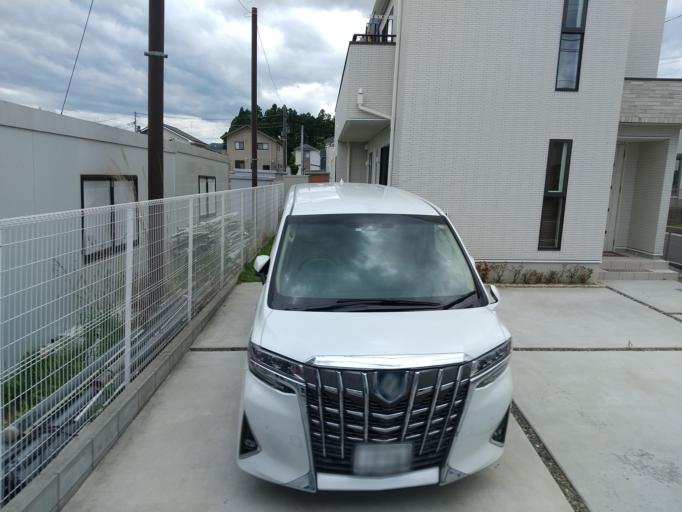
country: JP
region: Miyagi
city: Sendai
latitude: 38.2738
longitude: 140.7498
